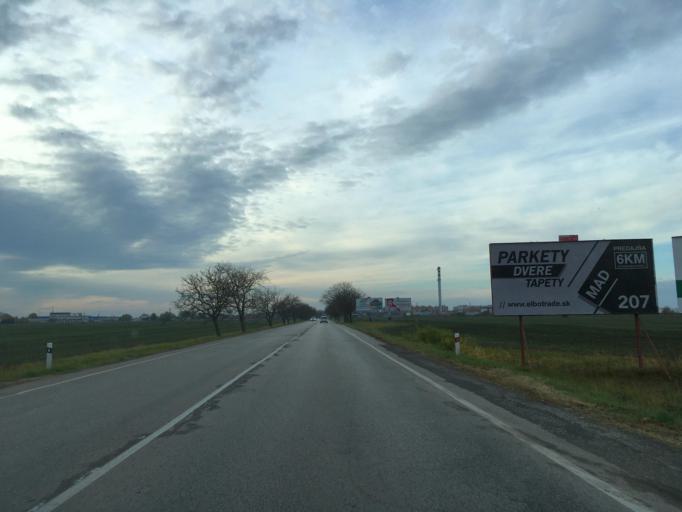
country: SK
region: Trnavsky
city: Dunajska Streda
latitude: 47.9826
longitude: 17.6453
